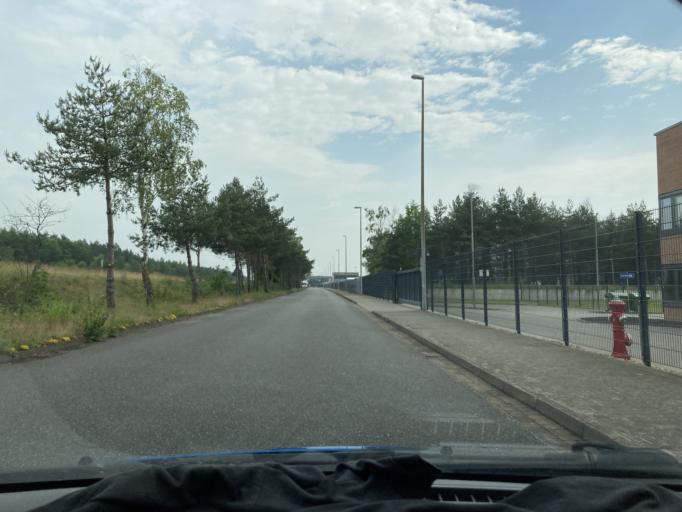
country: DE
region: Lower Saxony
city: Wendisch Evern
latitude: 53.2462
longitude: 10.4855
